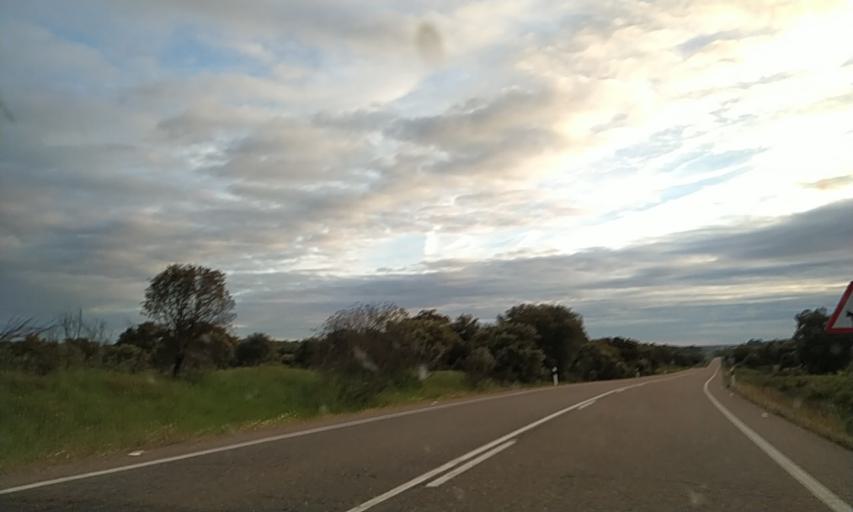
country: ES
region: Extremadura
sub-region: Provincia de Badajoz
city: La Roca de la Sierra
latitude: 39.1250
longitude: -6.6677
